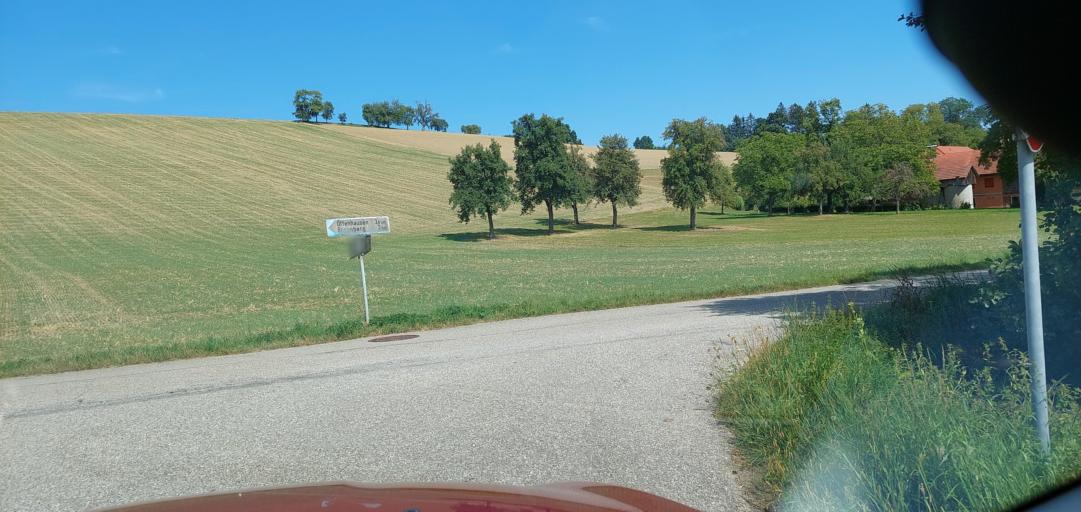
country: AT
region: Upper Austria
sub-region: Wels-Land
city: Pennewang
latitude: 48.1415
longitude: 13.8628
